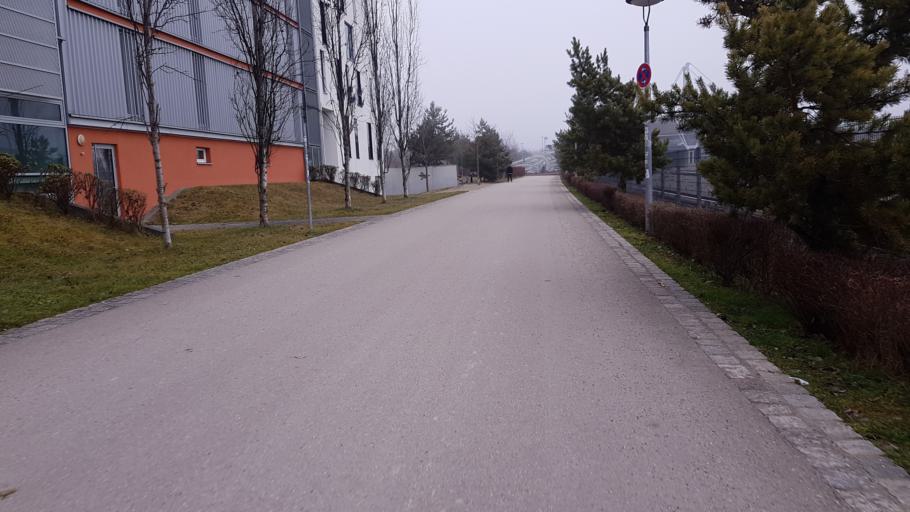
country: DE
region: Bavaria
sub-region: Upper Bavaria
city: Unterfoehring
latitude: 48.2095
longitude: 11.6152
